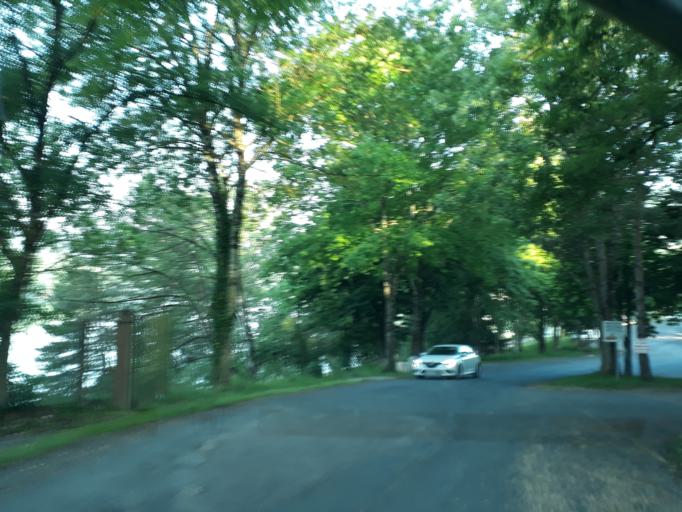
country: FR
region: Limousin
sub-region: Departement de la Correze
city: Saint-Pantaleon-de-Larche
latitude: 45.0986
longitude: 1.4636
